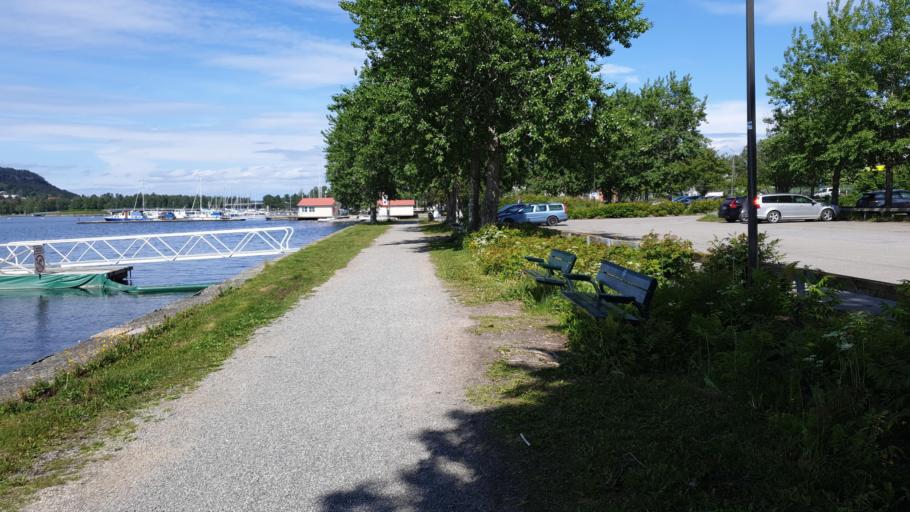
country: SE
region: Jaemtland
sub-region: OEstersunds Kommun
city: Ostersund
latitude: 63.1745
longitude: 14.6304
